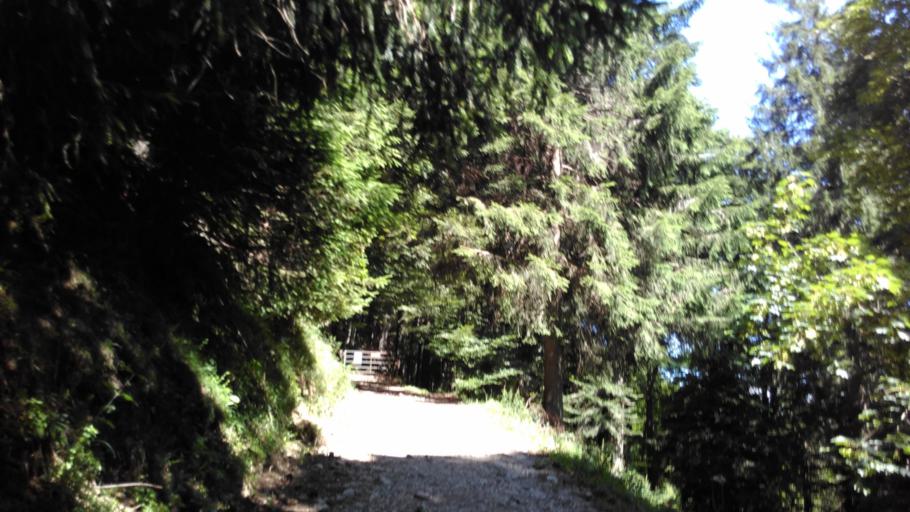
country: CH
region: Saint Gallen
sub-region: Wahlkreis See-Gaster
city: Goldingen
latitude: 47.2983
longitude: 9.0078
